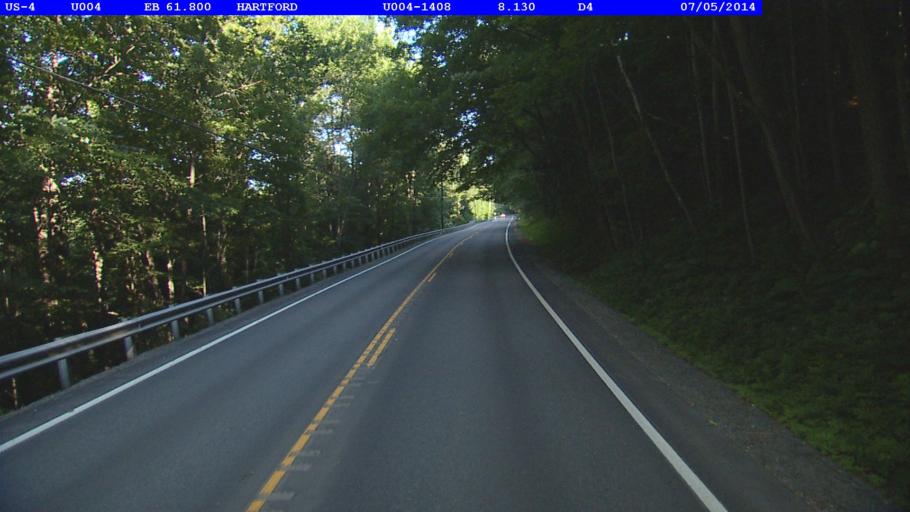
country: US
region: Vermont
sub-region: Windsor County
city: White River Junction
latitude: 43.6598
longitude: -72.3505
